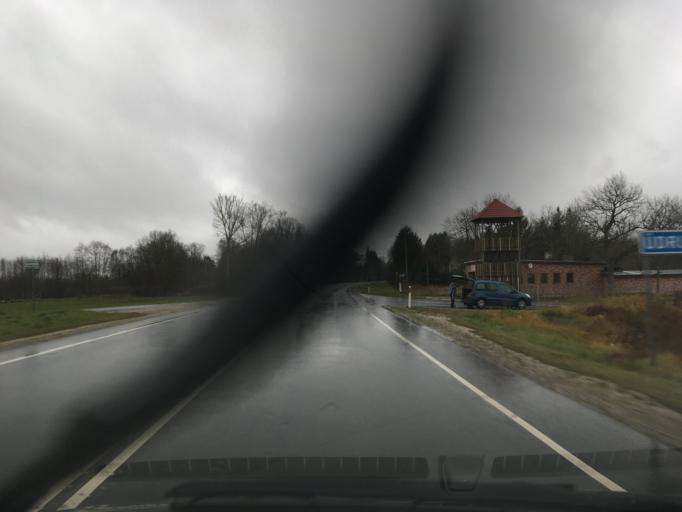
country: EE
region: Laeaene
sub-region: Lihula vald
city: Lihula
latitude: 58.8199
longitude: 24.0576
